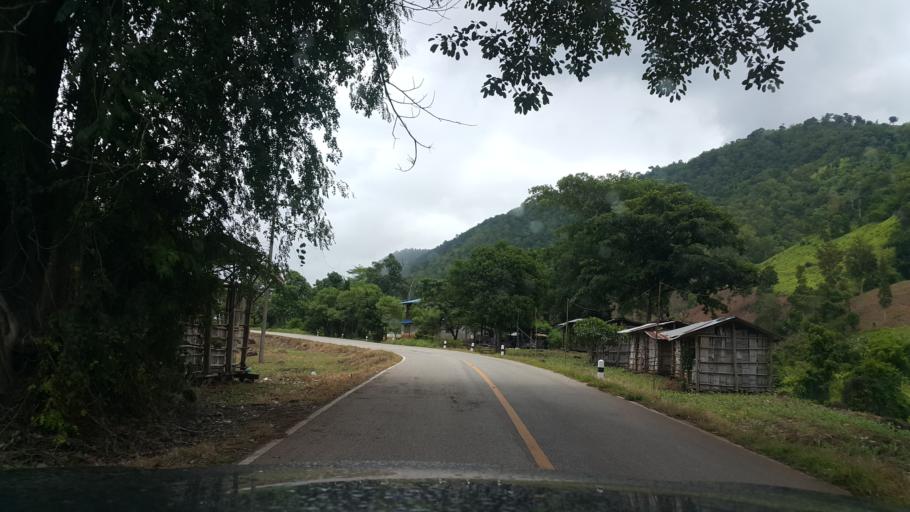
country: TH
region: Loei
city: Na Haeo
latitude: 17.5434
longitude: 100.8390
